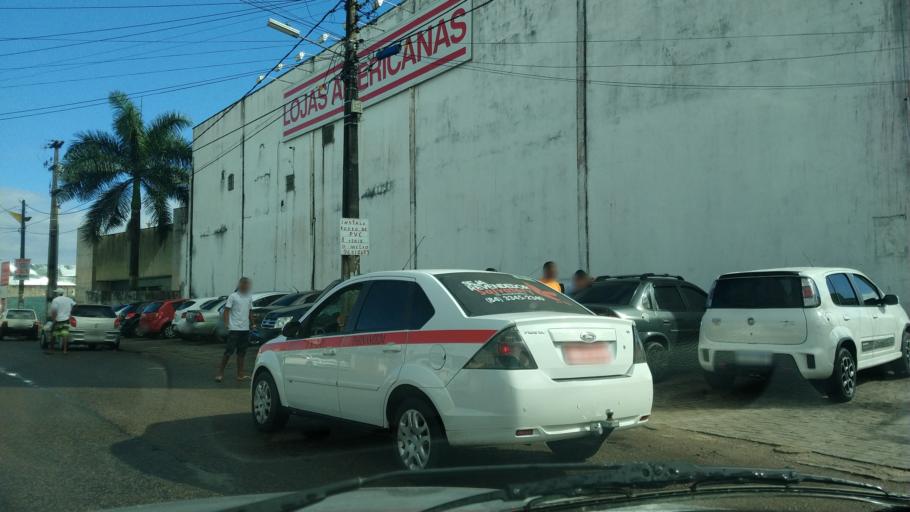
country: BR
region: Rio Grande do Norte
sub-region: Parnamirim
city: Parnamirim
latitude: -5.9147
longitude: -35.2615
